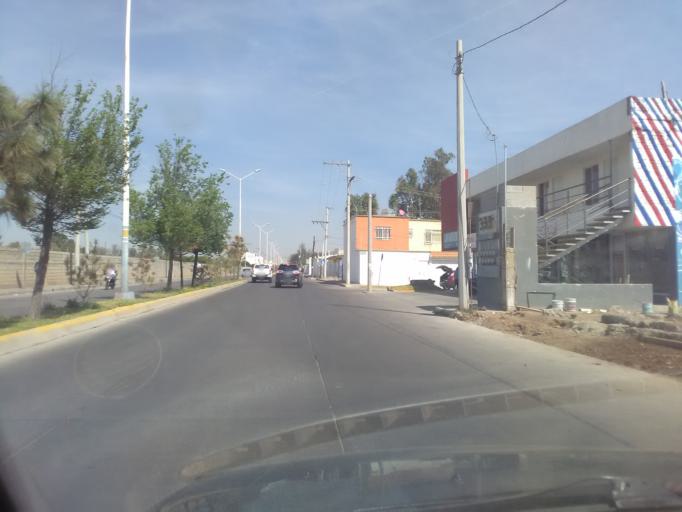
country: MX
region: Durango
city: Victoria de Durango
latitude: 24.0504
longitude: -104.6257
